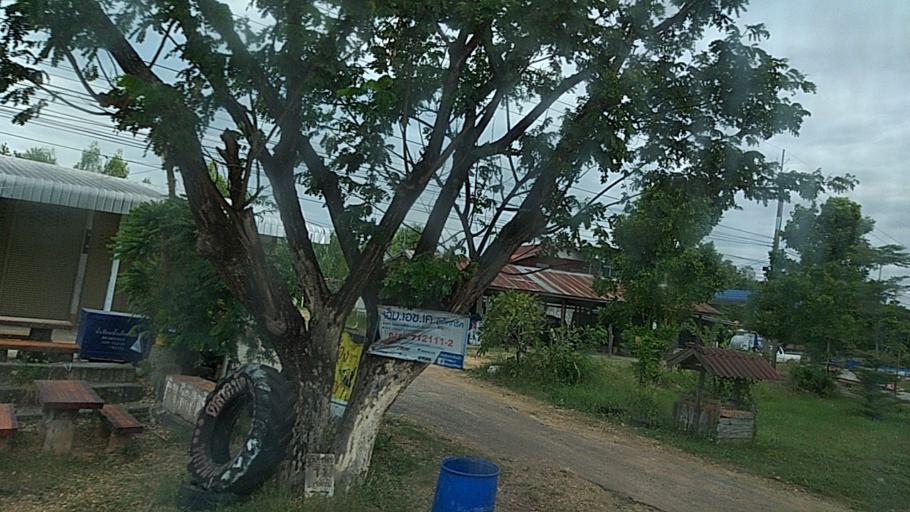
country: TH
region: Maha Sarakham
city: Kantharawichai
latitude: 16.3386
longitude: 103.1980
